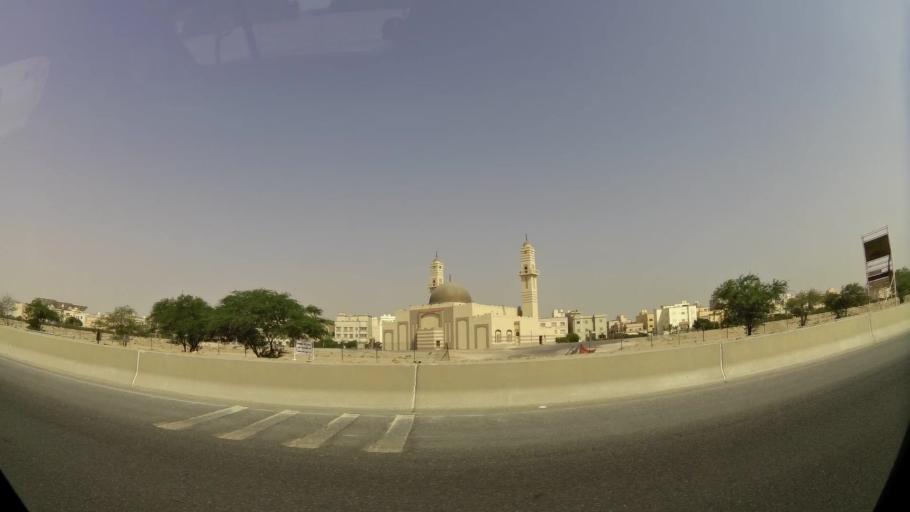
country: KW
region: Muhafazat al Jahra'
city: Al Jahra'
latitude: 29.3010
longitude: 47.6899
